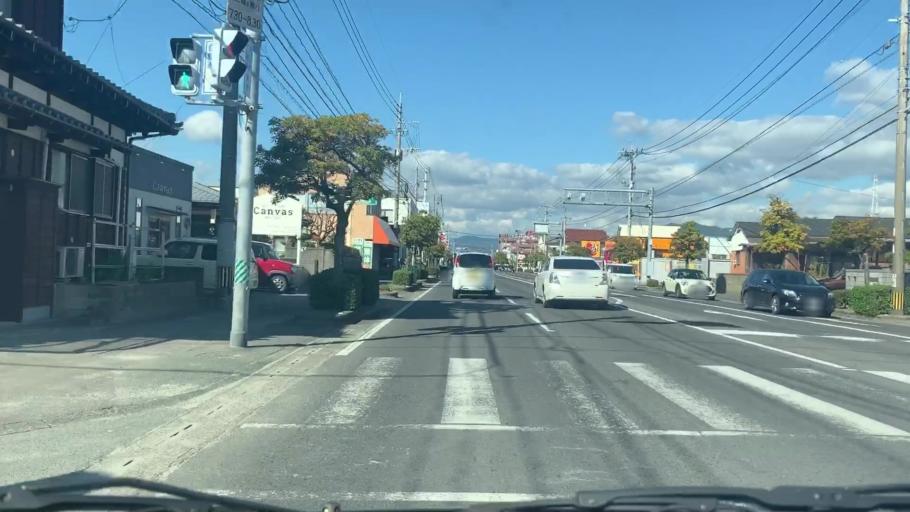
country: JP
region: Saga Prefecture
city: Saga-shi
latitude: 33.2847
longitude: 130.2909
